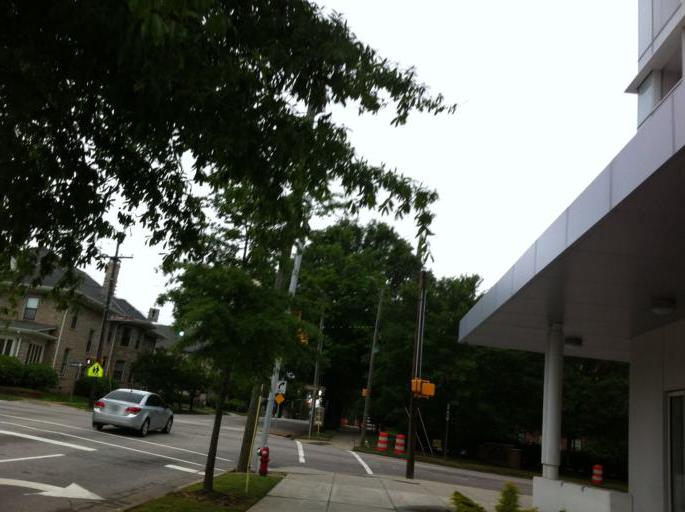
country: US
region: North Carolina
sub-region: Wake County
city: Raleigh
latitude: 35.7814
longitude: -78.6414
